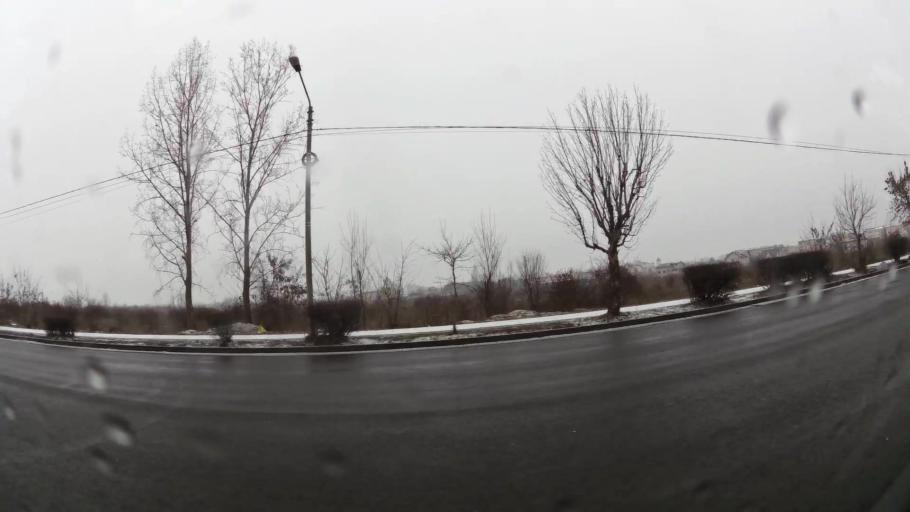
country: RO
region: Dambovita
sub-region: Municipiul Targoviste
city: Targoviste
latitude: 44.9106
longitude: 25.4703
